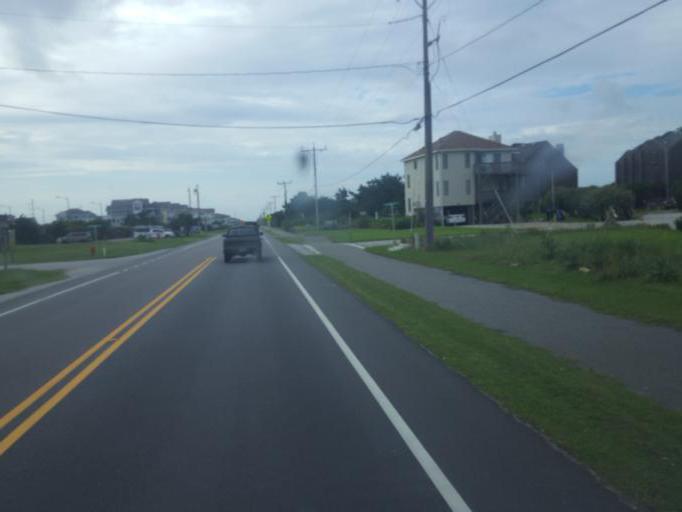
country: US
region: North Carolina
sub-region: Dare County
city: Nags Head
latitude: 35.9334
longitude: -75.6107
